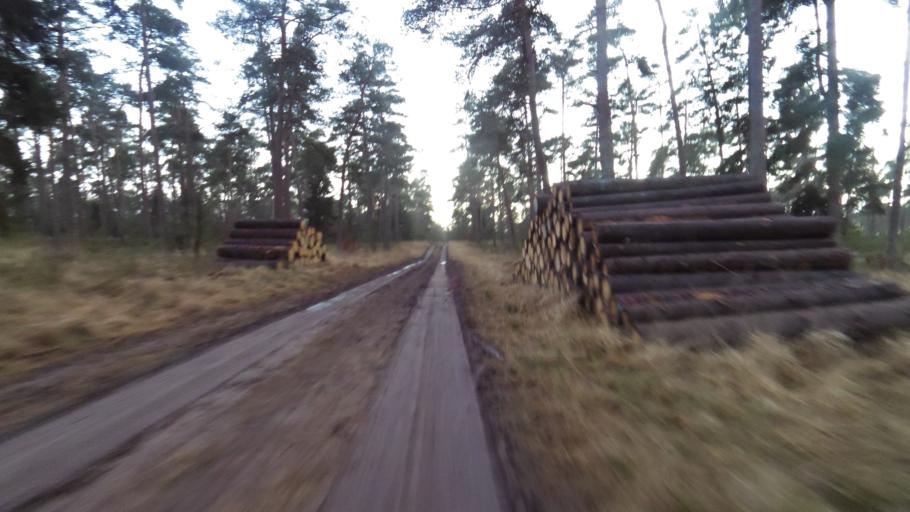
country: NL
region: Gelderland
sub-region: Gemeente Apeldoorn
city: Uddel
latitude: 52.2702
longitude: 5.8451
